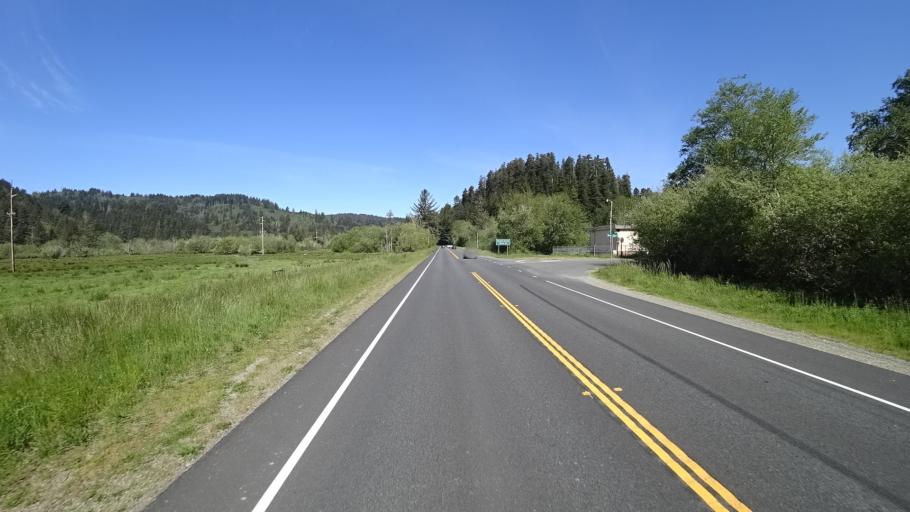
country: US
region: California
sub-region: Del Norte County
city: Bertsch-Oceanview
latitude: 41.5592
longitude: -124.0603
